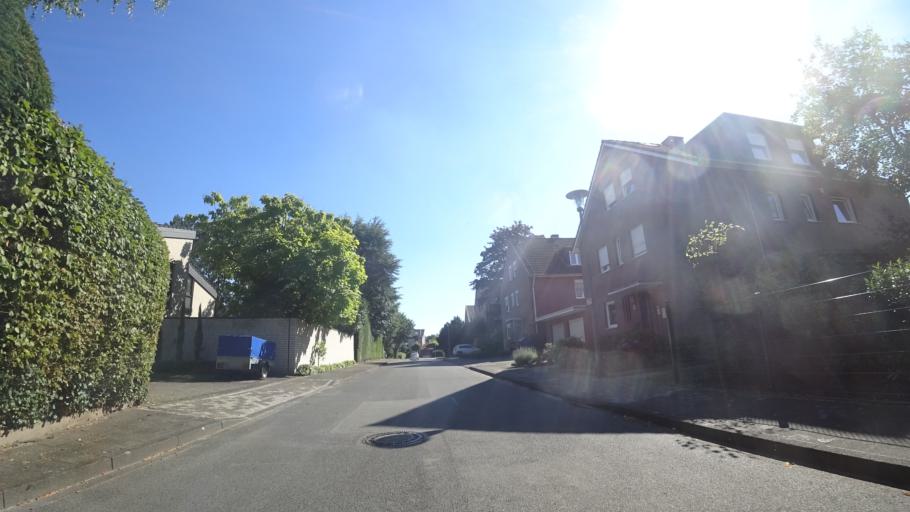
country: DE
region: North Rhine-Westphalia
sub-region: Regierungsbezirk Detmold
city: Guetersloh
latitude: 51.9205
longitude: 8.3882
